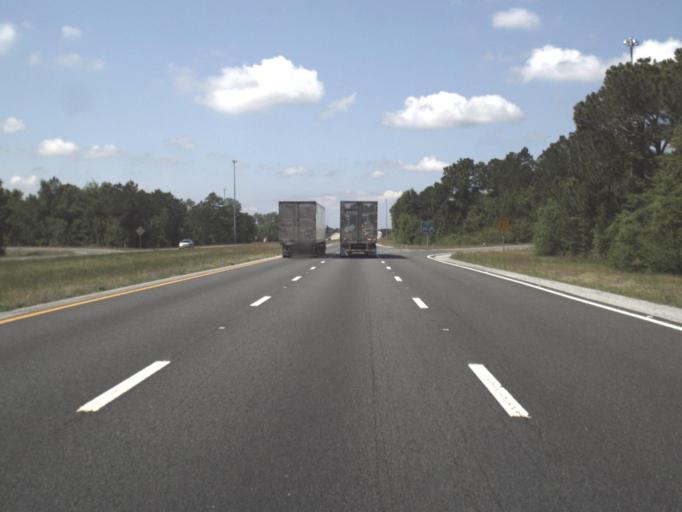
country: US
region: Florida
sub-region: Santa Rosa County
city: East Milton
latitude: 30.5937
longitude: -87.0008
